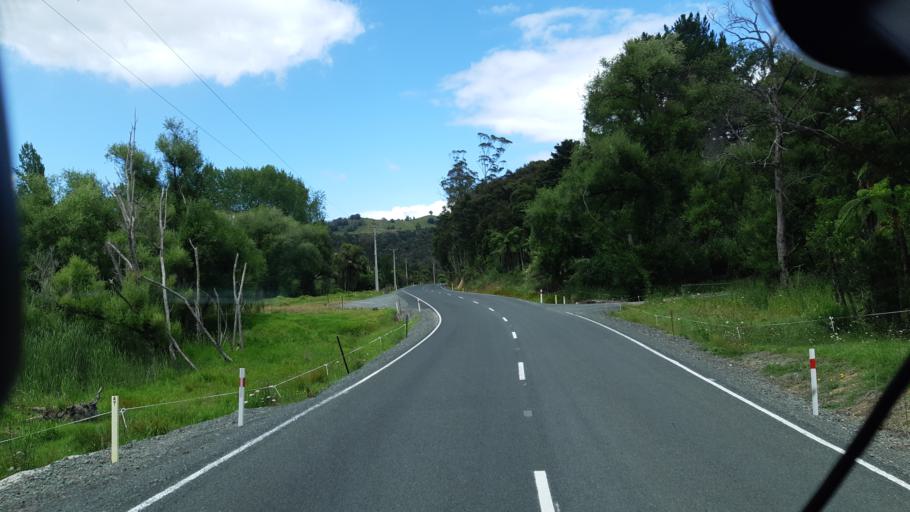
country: NZ
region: Northland
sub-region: Far North District
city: Taipa
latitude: -35.2402
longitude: 173.5412
